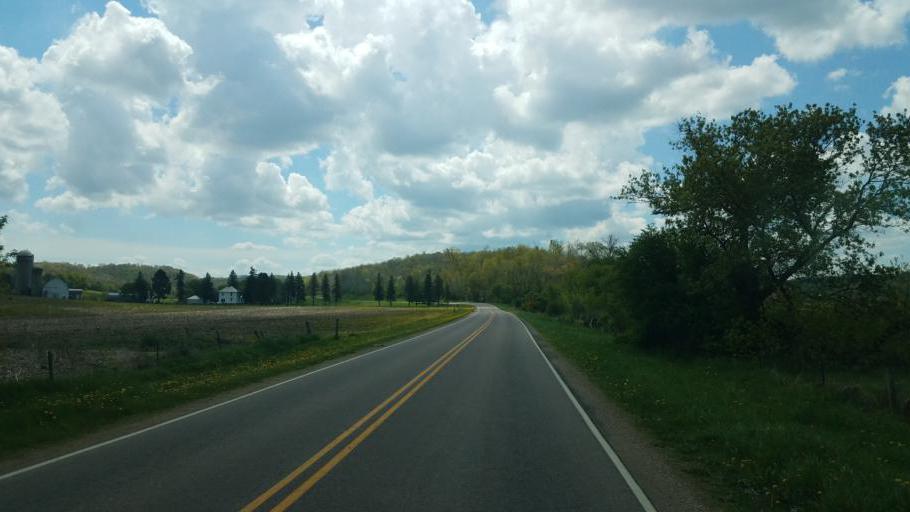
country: US
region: Wisconsin
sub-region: Vernon County
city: Hillsboro
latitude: 43.6374
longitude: -90.3526
